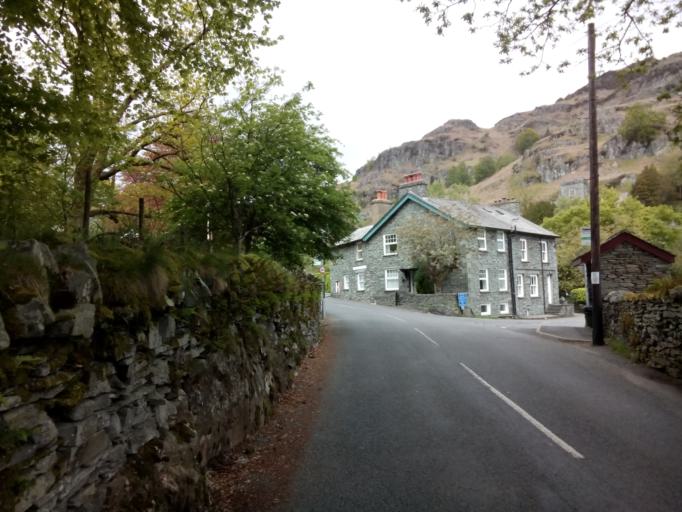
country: GB
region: England
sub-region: Cumbria
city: Ambleside
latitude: 54.4388
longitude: -3.0476
